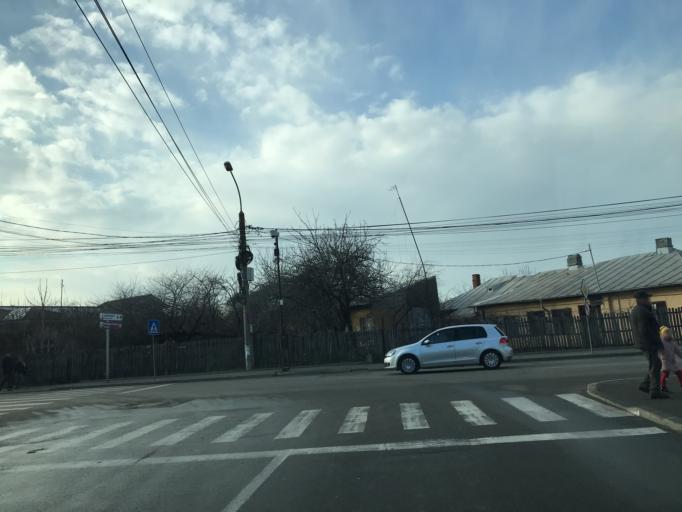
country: RO
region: Olt
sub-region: Municipiul Slatina
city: Slatina
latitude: 44.4271
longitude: 24.3631
